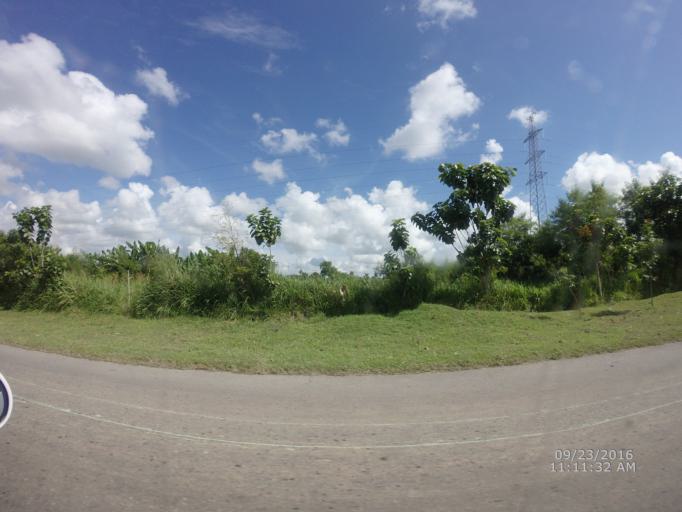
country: CU
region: La Habana
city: Arroyo Naranjo
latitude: 23.0257
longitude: -82.2705
